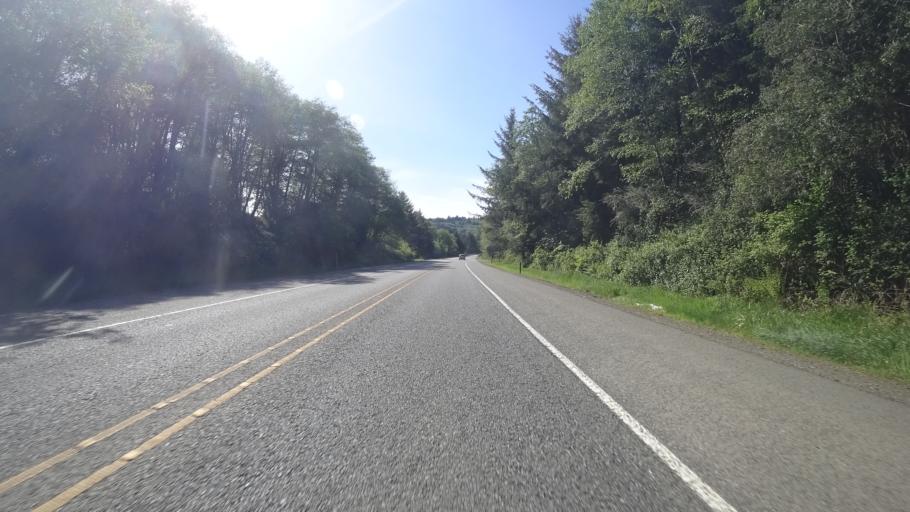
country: US
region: Oregon
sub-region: Curry County
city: Harbor
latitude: 42.0083
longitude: -124.2123
